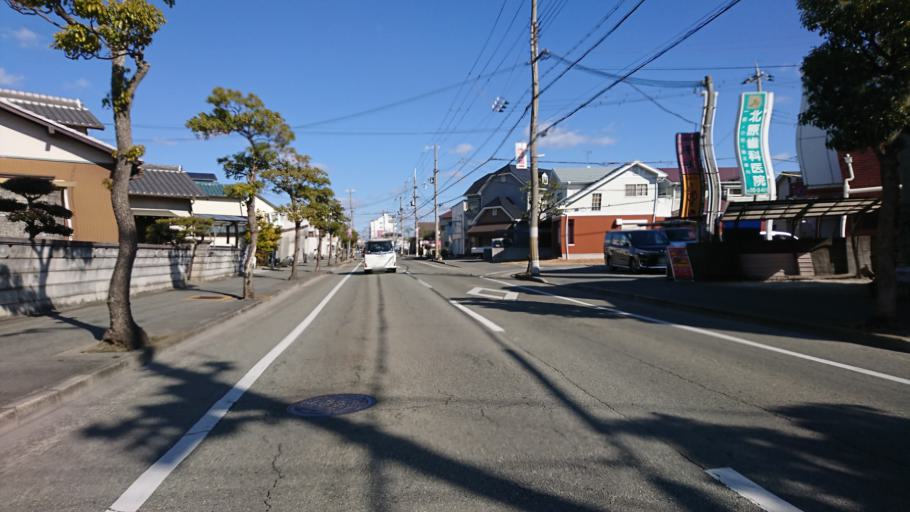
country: JP
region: Hyogo
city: Kakogawacho-honmachi
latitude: 34.7357
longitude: 134.8592
